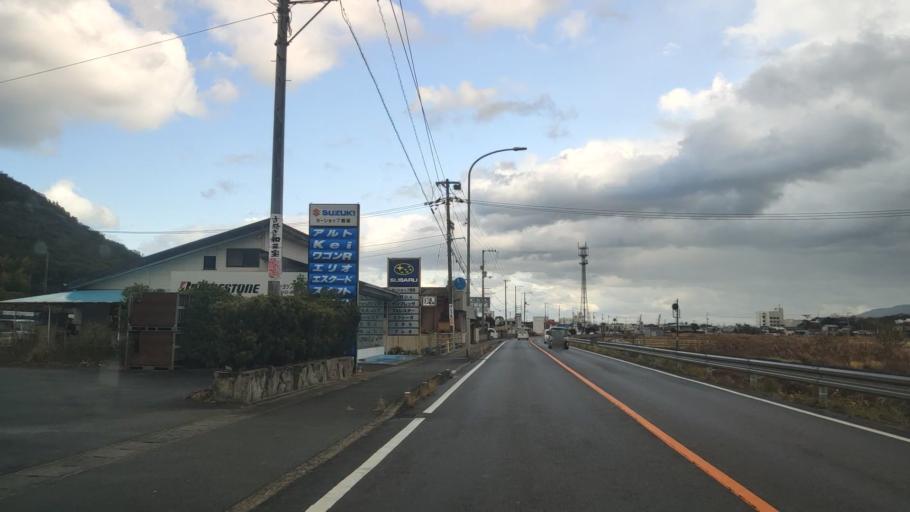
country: JP
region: Tokushima
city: Kamojimacho-jogejima
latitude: 34.2238
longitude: 134.3943
